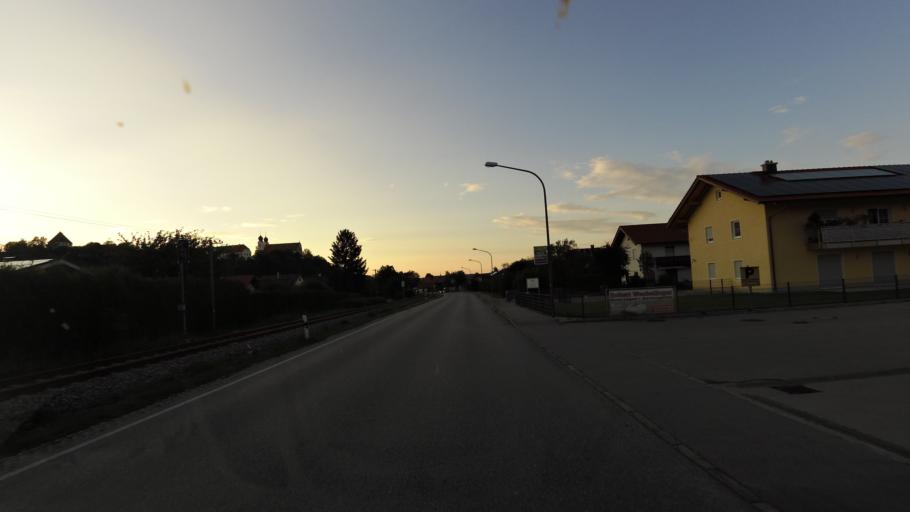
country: DE
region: Bavaria
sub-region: Upper Bavaria
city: Trostberg an der Alz
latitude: 47.9939
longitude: 12.5352
